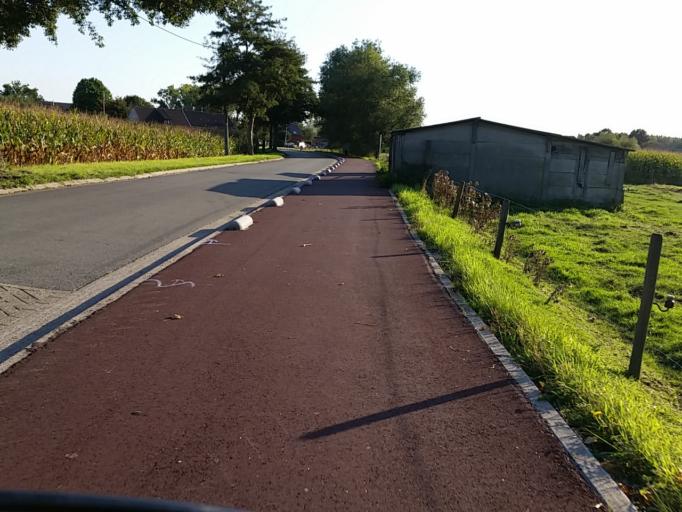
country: BE
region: Flanders
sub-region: Provincie Antwerpen
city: Mechelen
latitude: 51.0021
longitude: 4.4992
